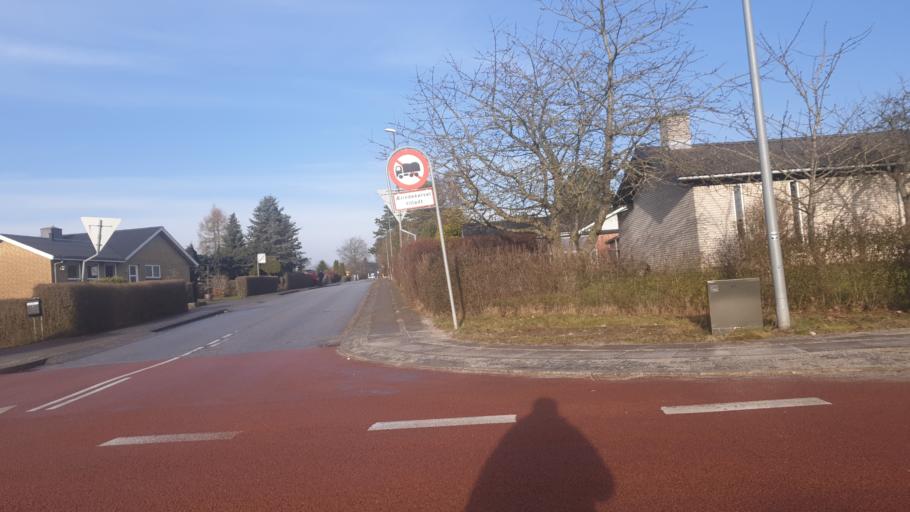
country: DK
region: Central Jutland
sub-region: Hedensted Kommune
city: Hedensted
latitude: 55.7759
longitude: 9.7157
